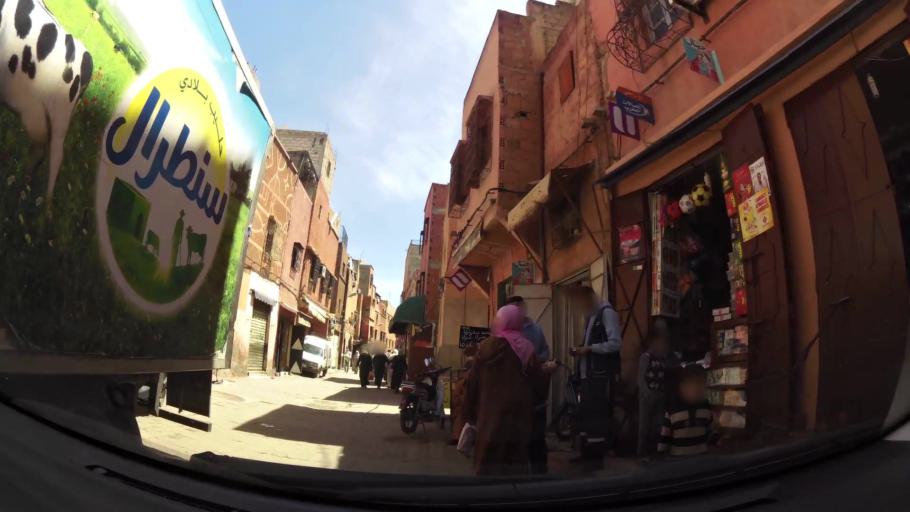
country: MA
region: Marrakech-Tensift-Al Haouz
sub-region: Marrakech
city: Marrakesh
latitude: 31.6195
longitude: -7.9682
